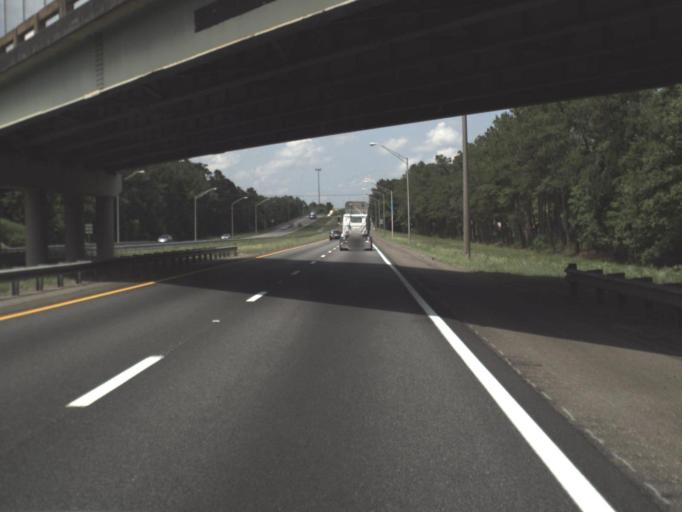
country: US
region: Florida
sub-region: Duval County
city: Jacksonville
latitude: 30.4012
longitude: -81.7547
